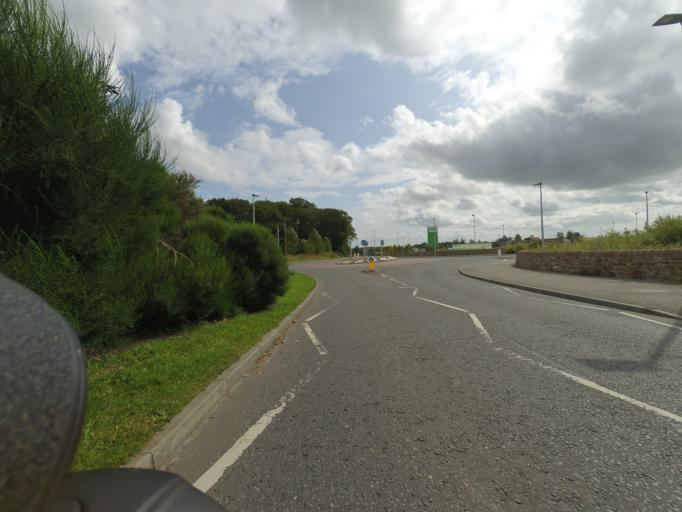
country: GB
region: Scotland
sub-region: Highland
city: Tain
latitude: 57.8049
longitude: -4.0465
